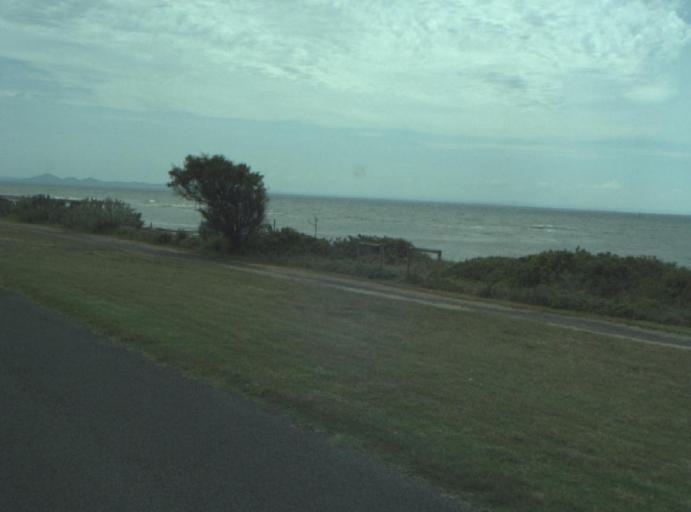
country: AU
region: Victoria
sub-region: Greater Geelong
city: Clifton Springs
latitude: -38.1167
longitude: 144.6804
